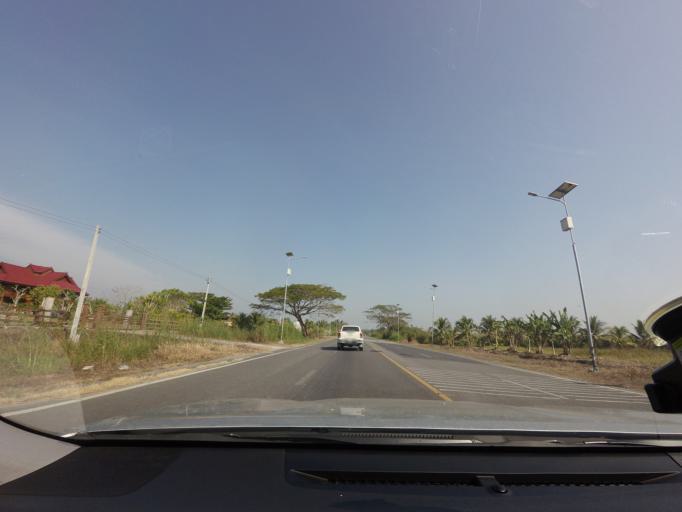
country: TH
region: Nakhon Si Thammarat
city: Nakhon Si Thammarat
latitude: 8.4775
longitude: 99.9781
